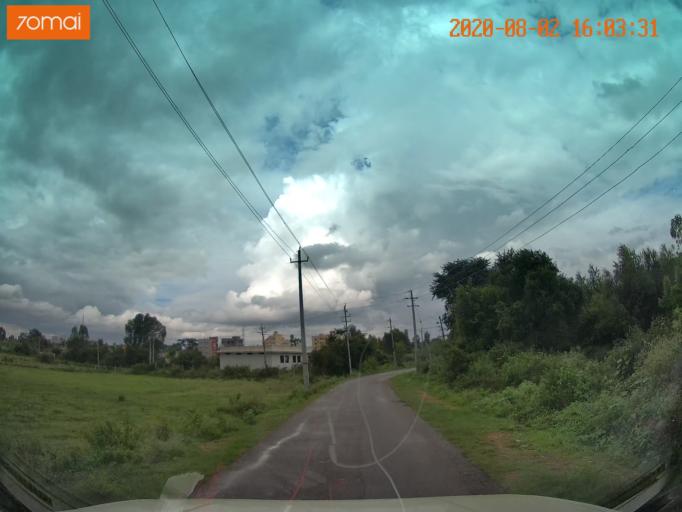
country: IN
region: Karnataka
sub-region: Bangalore Urban
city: Anekal
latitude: 12.8296
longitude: 77.6354
